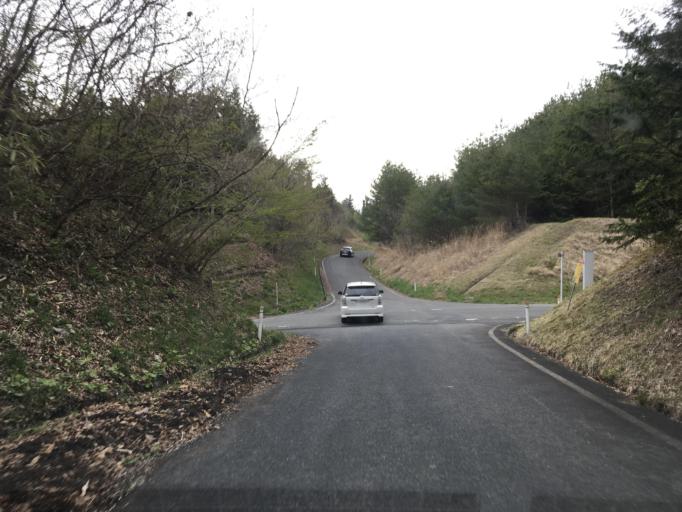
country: JP
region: Iwate
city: Ichinoseki
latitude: 38.8431
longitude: 141.3335
